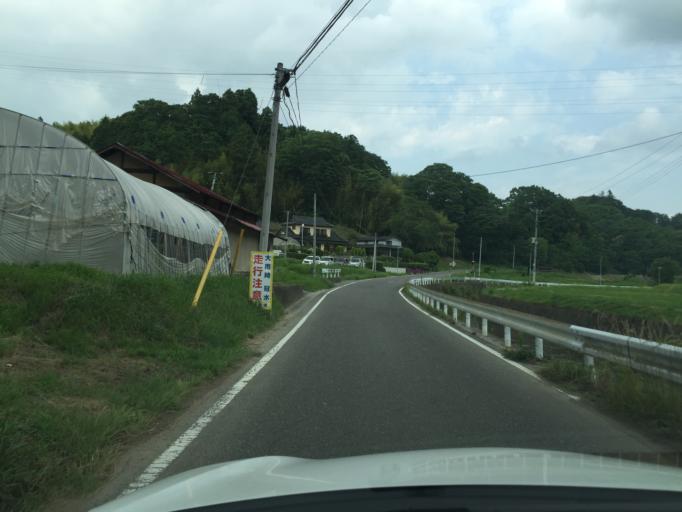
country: JP
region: Fukushima
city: Sukagawa
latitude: 37.3338
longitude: 140.4667
